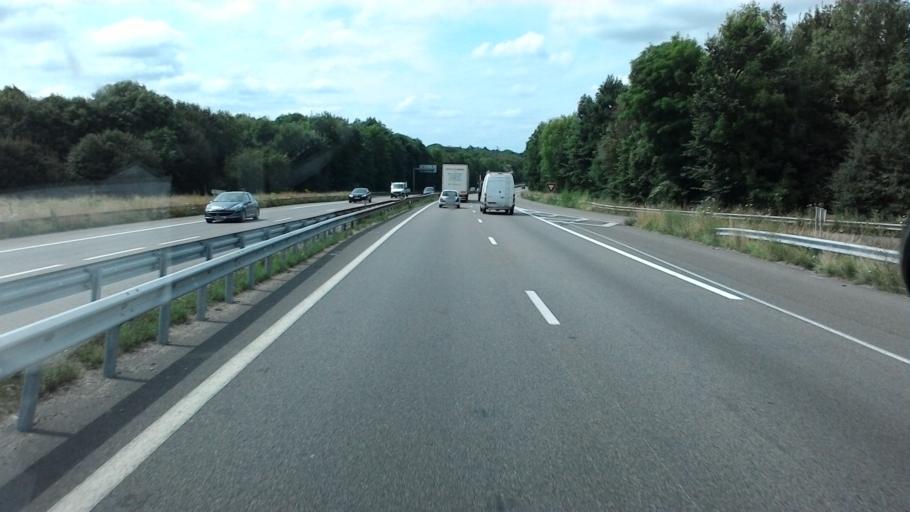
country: FR
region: Lorraine
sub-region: Departement de Meurthe-et-Moselle
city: Chavigny
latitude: 48.6469
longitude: 6.1390
